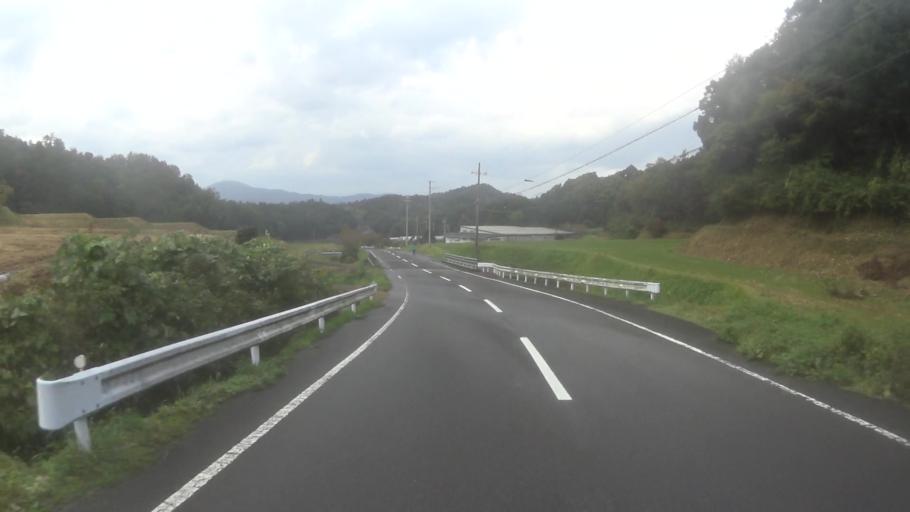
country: JP
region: Kyoto
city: Miyazu
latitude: 35.5036
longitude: 135.1308
